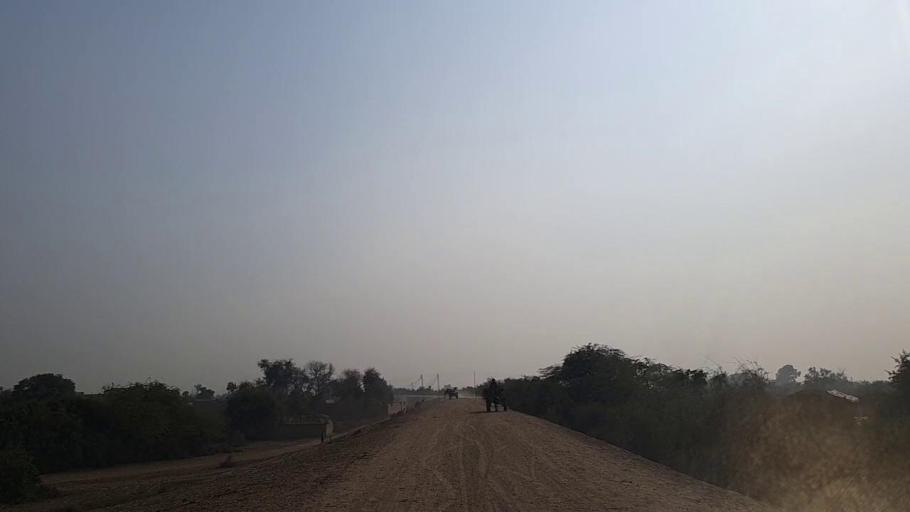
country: PK
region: Sindh
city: Sann
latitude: 26.0988
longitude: 68.1472
